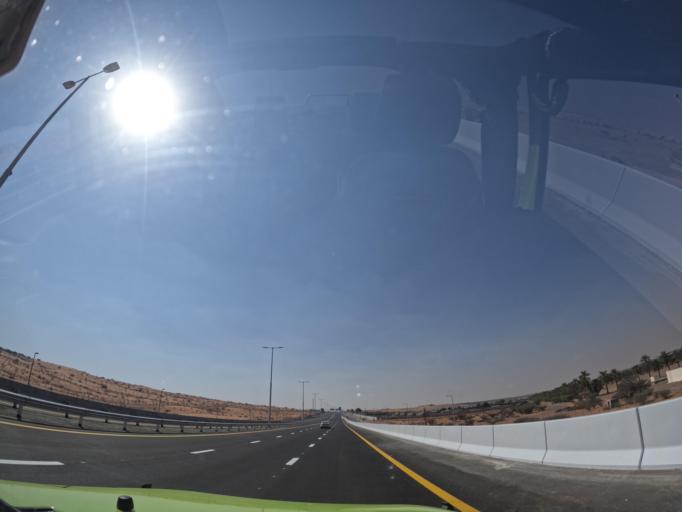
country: OM
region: Al Buraimi
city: Al Buraymi
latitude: 24.7617
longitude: 55.8066
